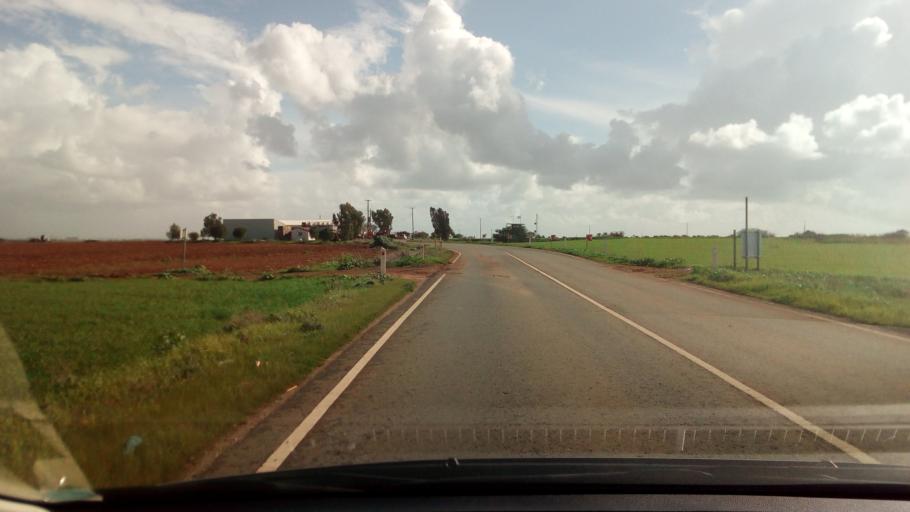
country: CY
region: Ammochostos
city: Achna
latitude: 35.0610
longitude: 33.8030
